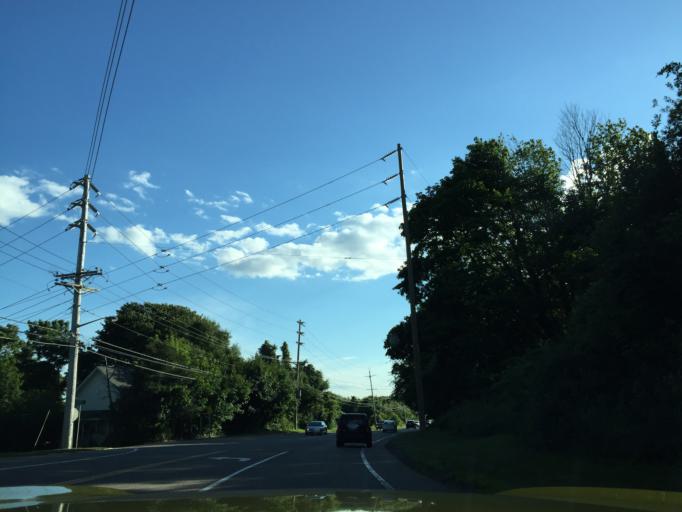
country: US
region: New York
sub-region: Suffolk County
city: Greenport West
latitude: 41.0992
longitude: -72.3899
